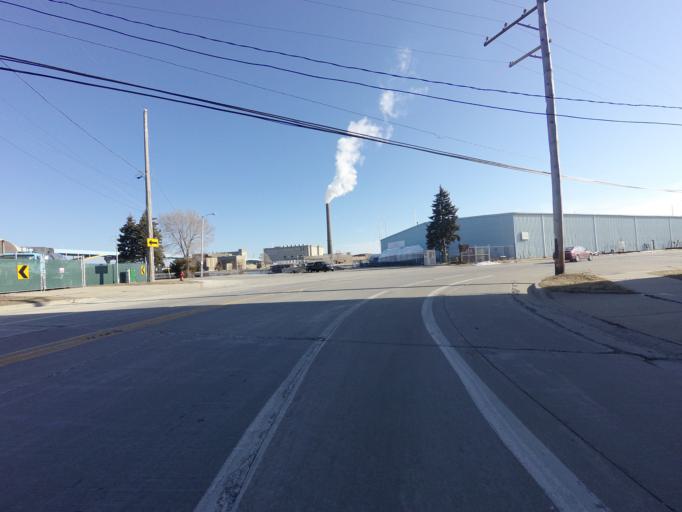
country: US
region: Wisconsin
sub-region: Milwaukee County
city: Milwaukee
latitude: 43.0255
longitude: -87.9047
